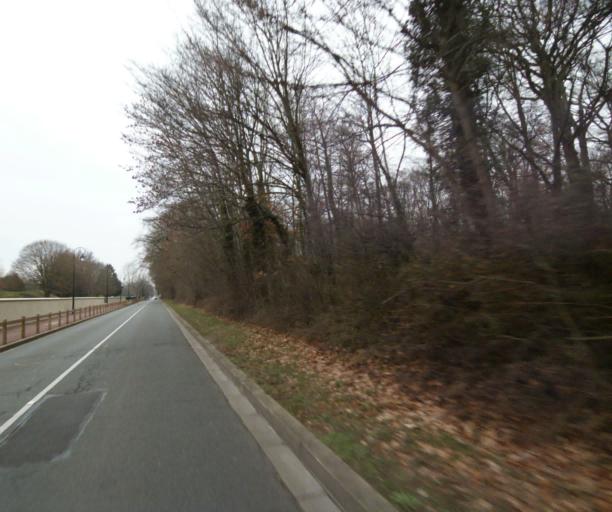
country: FR
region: Ile-de-France
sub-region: Departement des Hauts-de-Seine
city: Vaucresson
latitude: 48.8468
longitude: 2.1636
